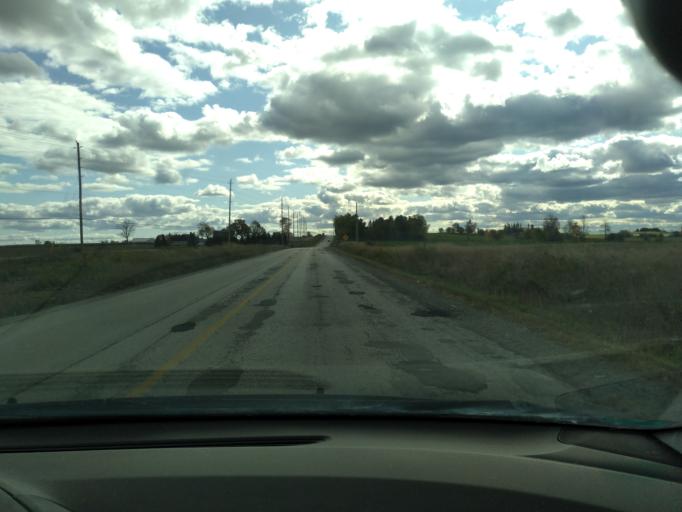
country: CA
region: Ontario
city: Bradford West Gwillimbury
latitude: 44.0913
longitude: -79.5980
